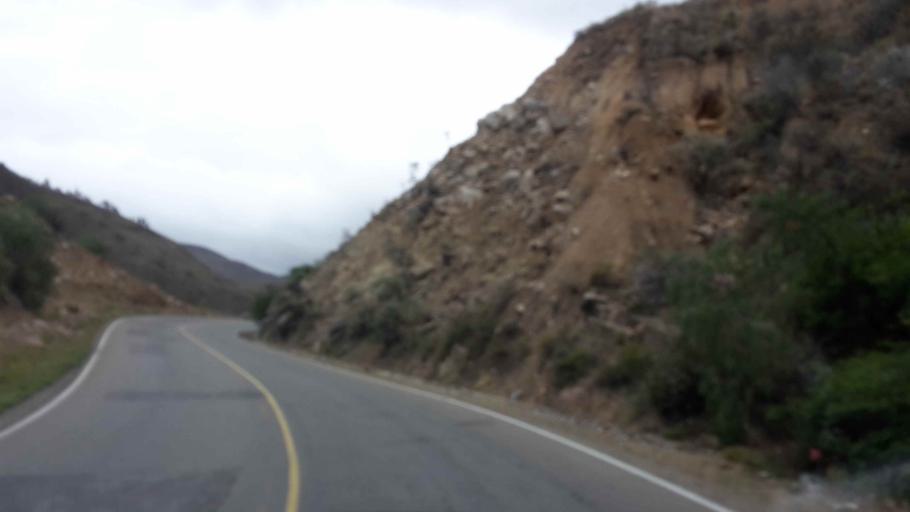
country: BO
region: Cochabamba
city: Punata
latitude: -17.4988
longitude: -65.7944
